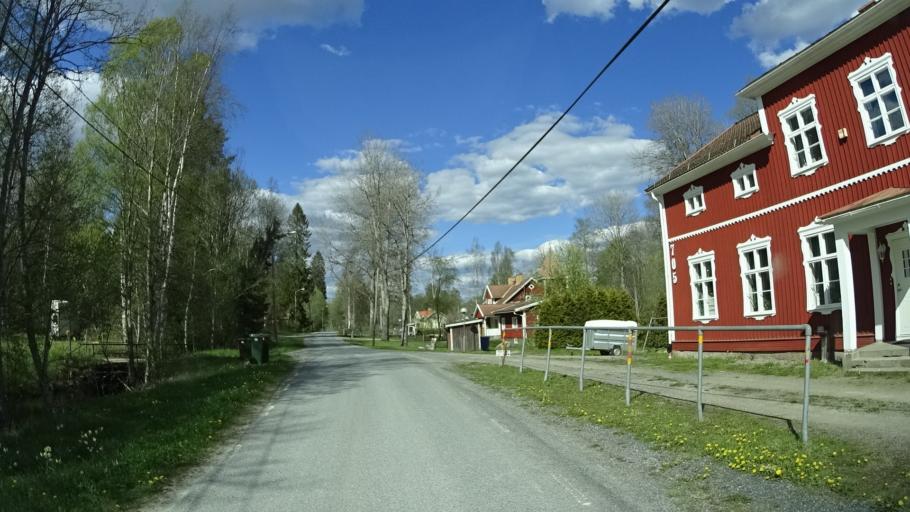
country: SE
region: OErebro
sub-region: Orebro Kommun
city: Garphyttan
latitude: 59.4325
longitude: 14.8643
